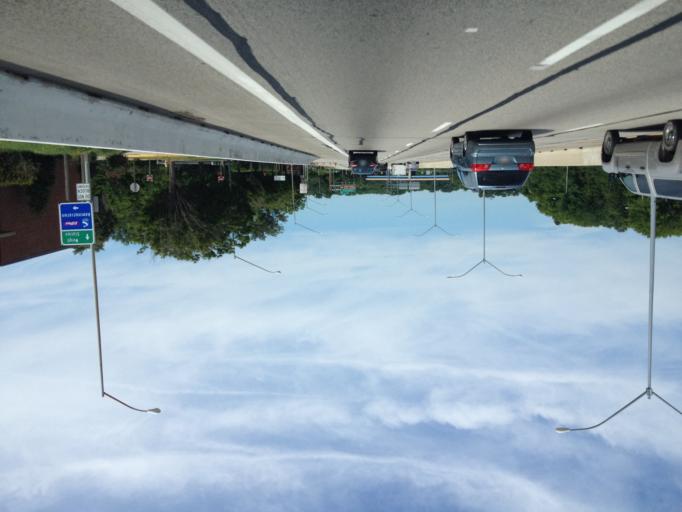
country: US
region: Maryland
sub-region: Anne Arundel County
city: Cape Saint Claire
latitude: 39.0131
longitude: -76.4068
